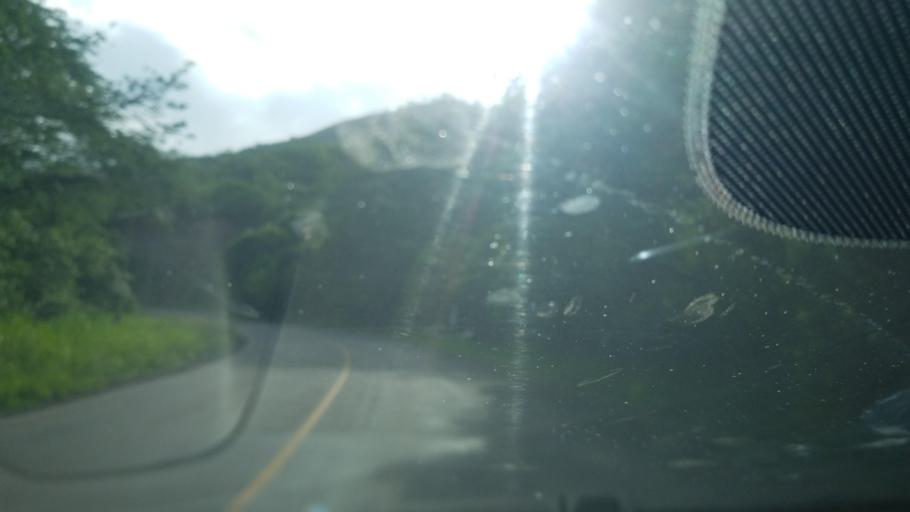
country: HN
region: Santa Barbara
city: Ilama
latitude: 15.0905
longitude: -88.2084
